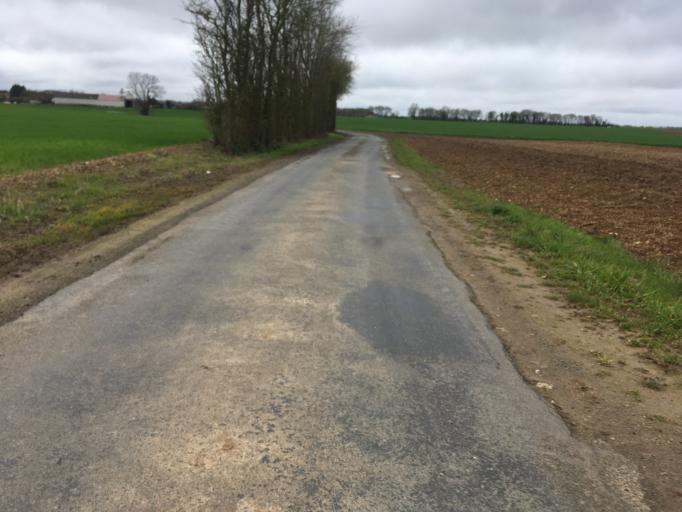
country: FR
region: Poitou-Charentes
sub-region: Departement de la Charente-Maritime
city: Saint-Germain-de-Marencennes
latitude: 46.1156
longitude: -0.8230
